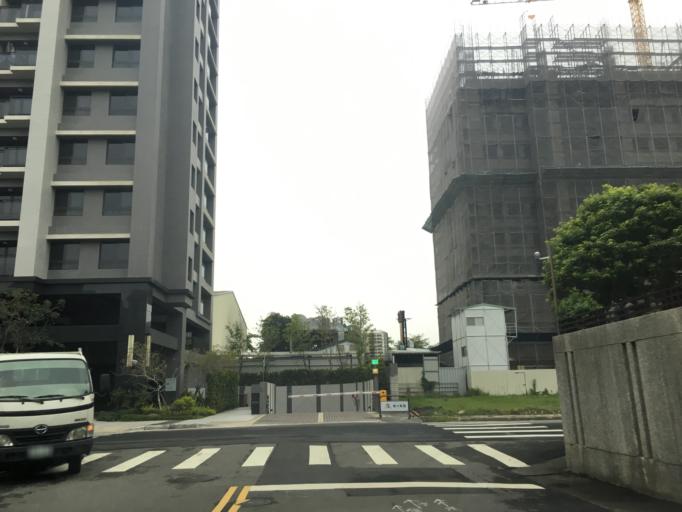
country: TW
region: Taiwan
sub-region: Taichung City
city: Taichung
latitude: 24.1656
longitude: 120.7073
